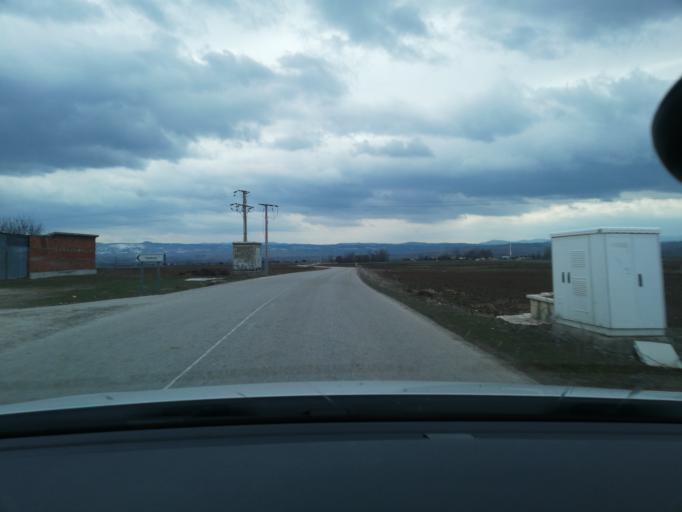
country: TR
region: Bolu
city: Gerede
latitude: 40.7545
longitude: 32.2037
